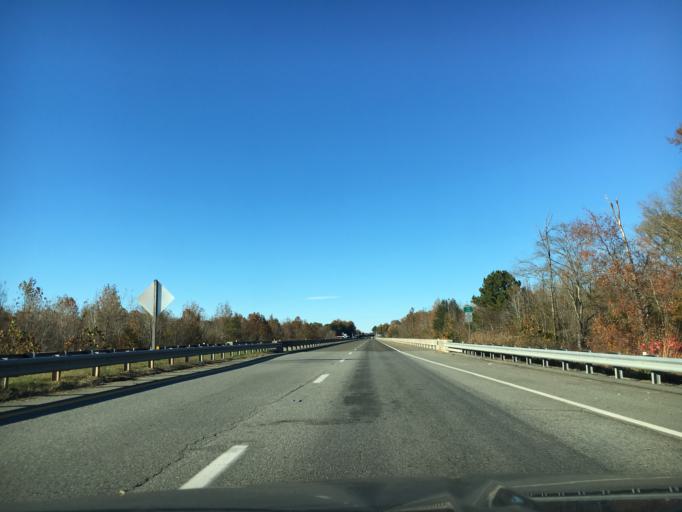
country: US
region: Virginia
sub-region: Halifax County
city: South Boston
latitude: 36.6906
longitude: -78.8872
